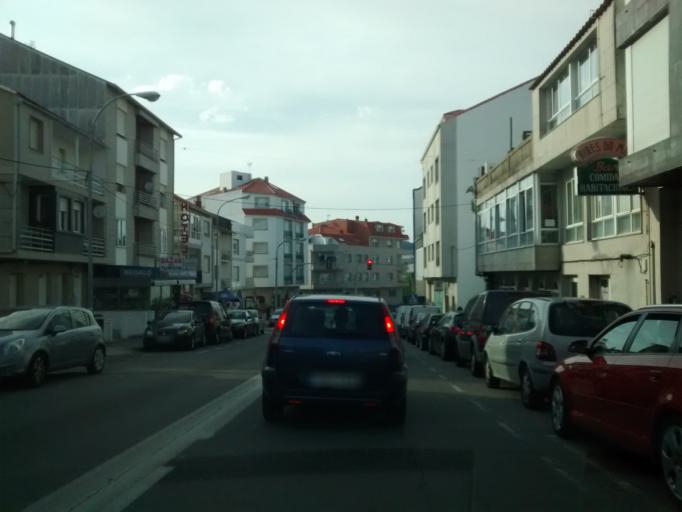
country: ES
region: Galicia
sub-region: Provincia de Pontevedra
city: Sanxenxo
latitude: 42.3948
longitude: -8.8290
